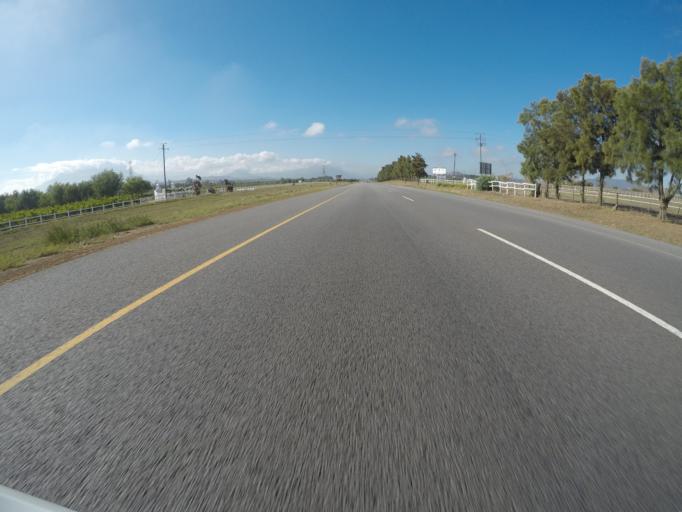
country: ZA
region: Western Cape
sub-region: City of Cape Town
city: Kraaifontein
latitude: -33.8468
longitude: 18.8034
